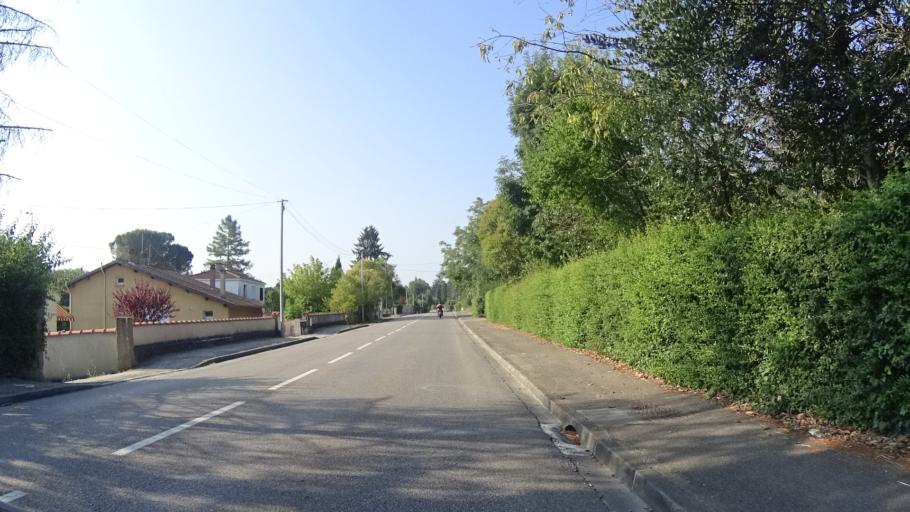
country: FR
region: Midi-Pyrenees
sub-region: Departement de l'Ariege
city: Mirepoix
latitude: 43.0822
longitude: 1.8765
